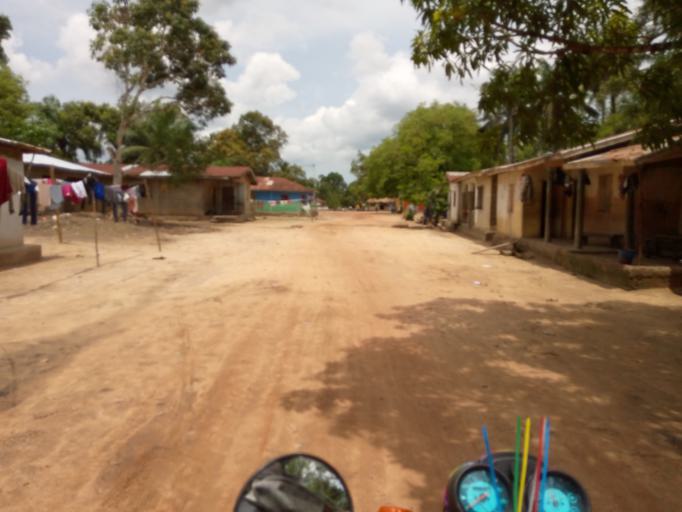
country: SL
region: Western Area
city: Waterloo
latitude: 8.3163
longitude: -12.9419
